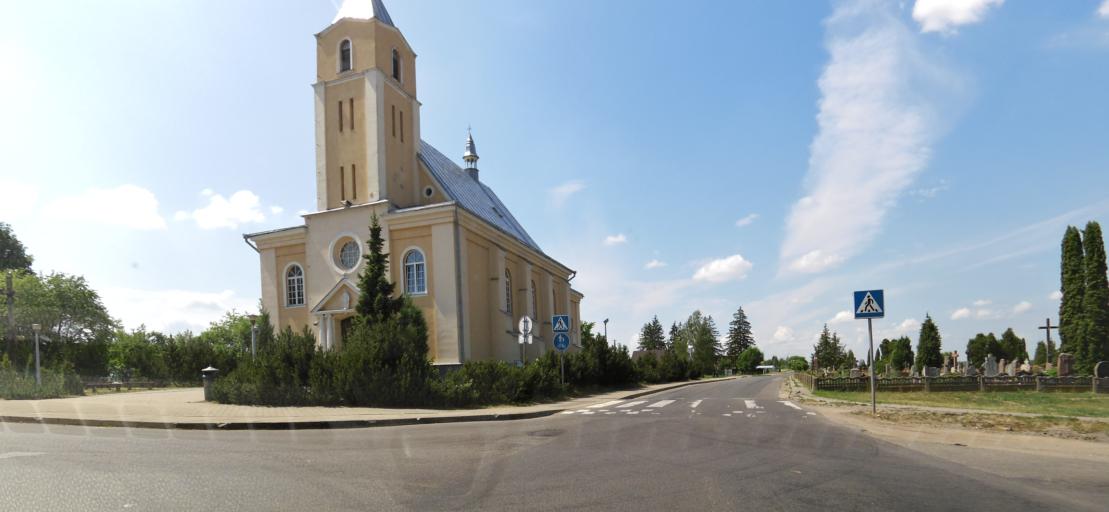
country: LT
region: Vilnius County
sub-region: Vilnius
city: Fabijoniskes
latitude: 54.8073
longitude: 25.2566
